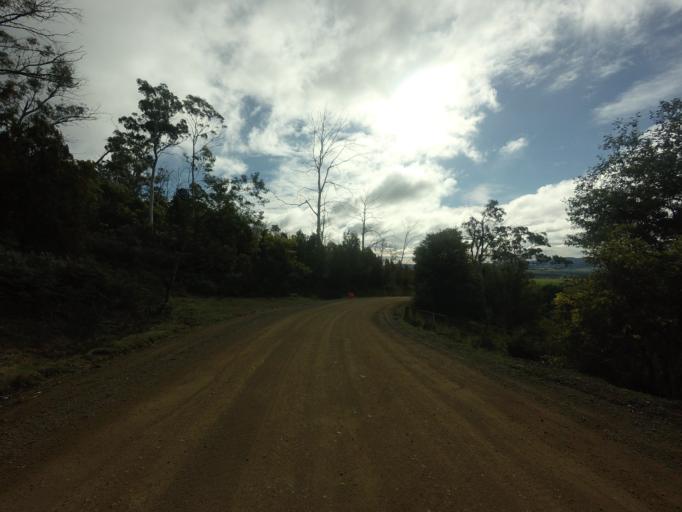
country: AU
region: Tasmania
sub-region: Derwent Valley
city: New Norfolk
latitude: -42.7244
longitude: 146.8717
